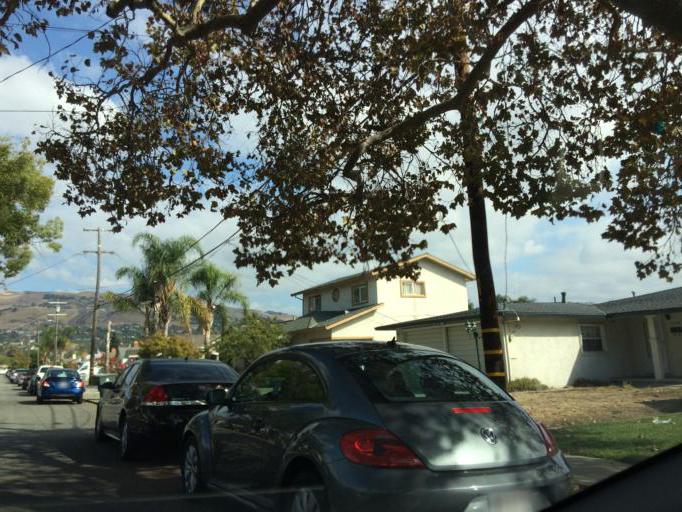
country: US
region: California
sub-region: Santa Clara County
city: Alum Rock
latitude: 37.3720
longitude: -121.8321
